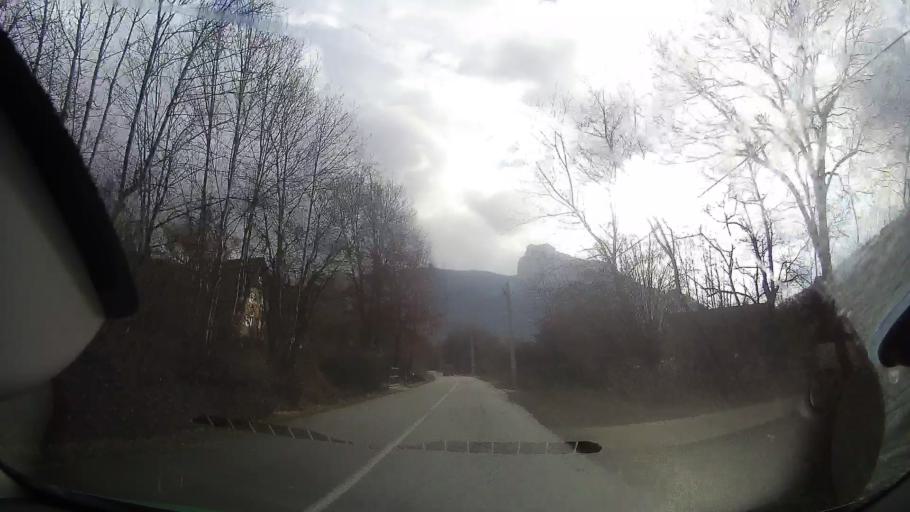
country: RO
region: Alba
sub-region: Comuna Rimetea
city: Rimetea
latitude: 46.4764
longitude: 23.5839
